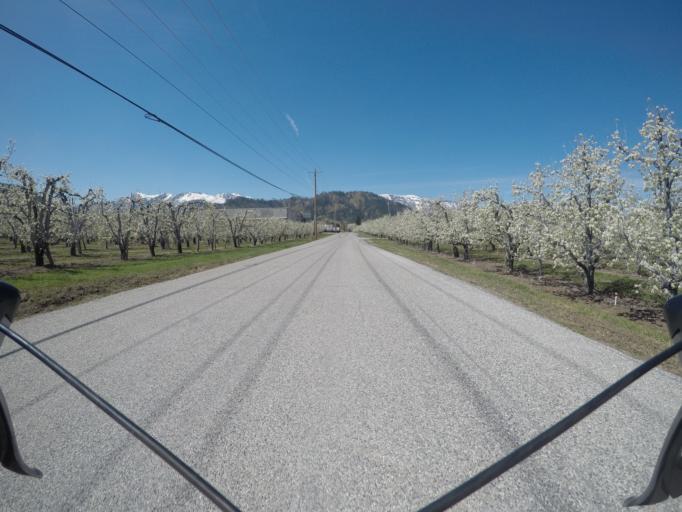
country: US
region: Washington
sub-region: Chelan County
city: Leavenworth
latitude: 47.5642
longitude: -120.5834
